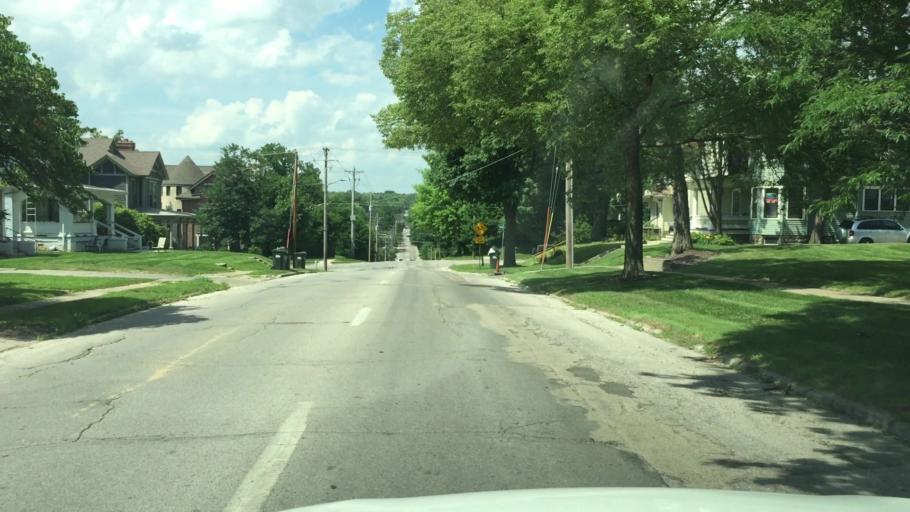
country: US
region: Iowa
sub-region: Johnson County
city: Iowa City
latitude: 41.6592
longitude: -91.5229
